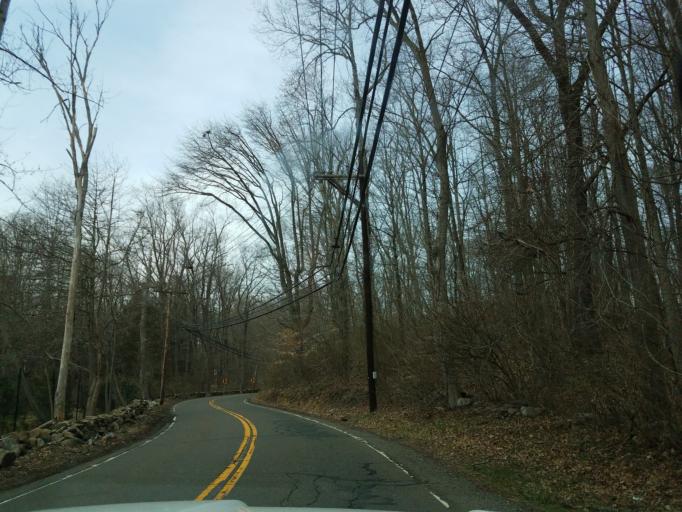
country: US
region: New York
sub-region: Westchester County
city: Armonk
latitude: 41.1058
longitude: -73.6530
